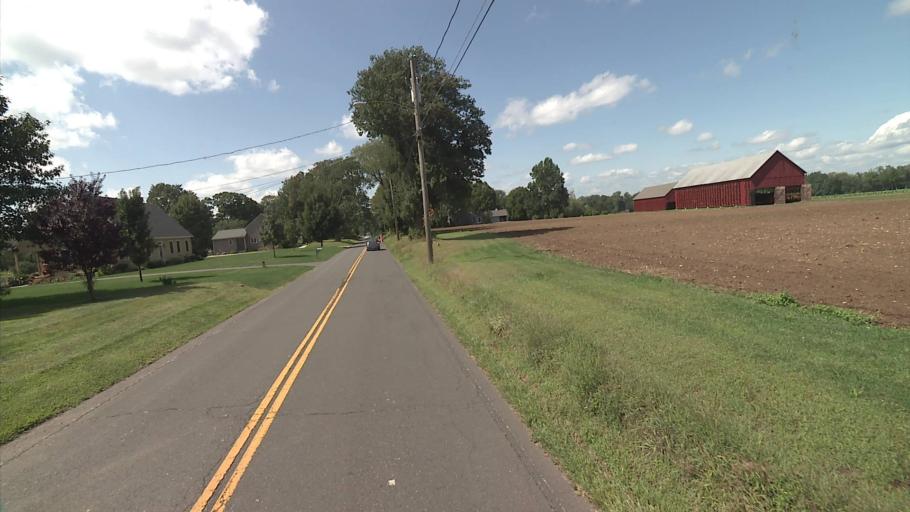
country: US
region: Connecticut
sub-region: Hartford County
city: Glastonbury Center
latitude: 41.6640
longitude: -72.6172
